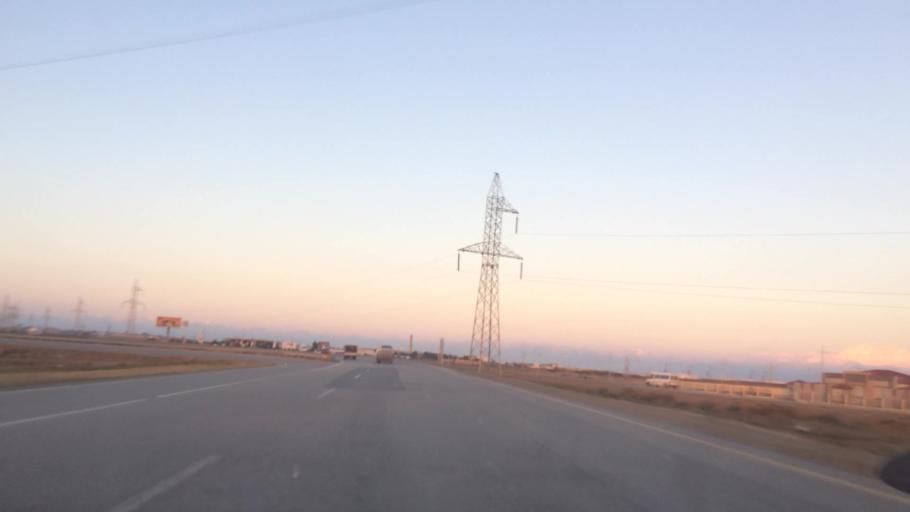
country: AZ
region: Baki
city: Qobustan
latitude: 39.9661
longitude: 49.4104
